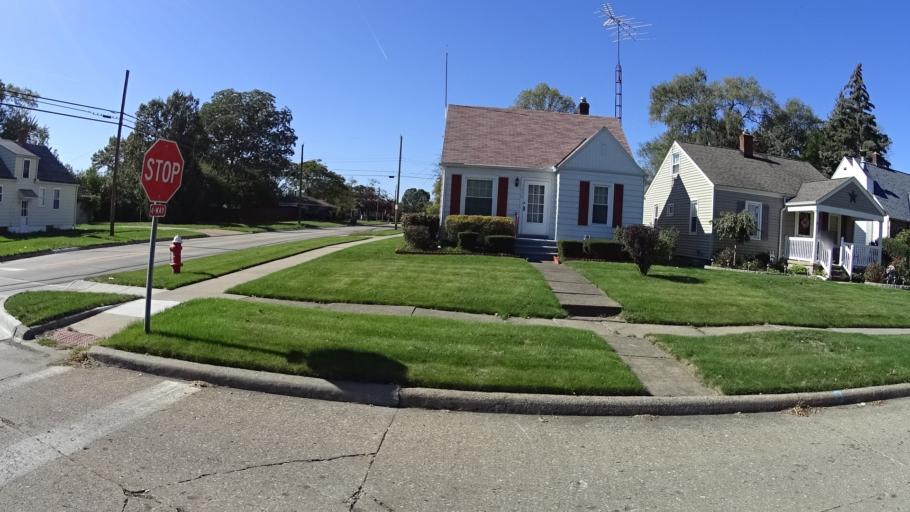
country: US
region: Ohio
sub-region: Lorain County
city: Lorain
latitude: 41.4401
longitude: -82.1698
